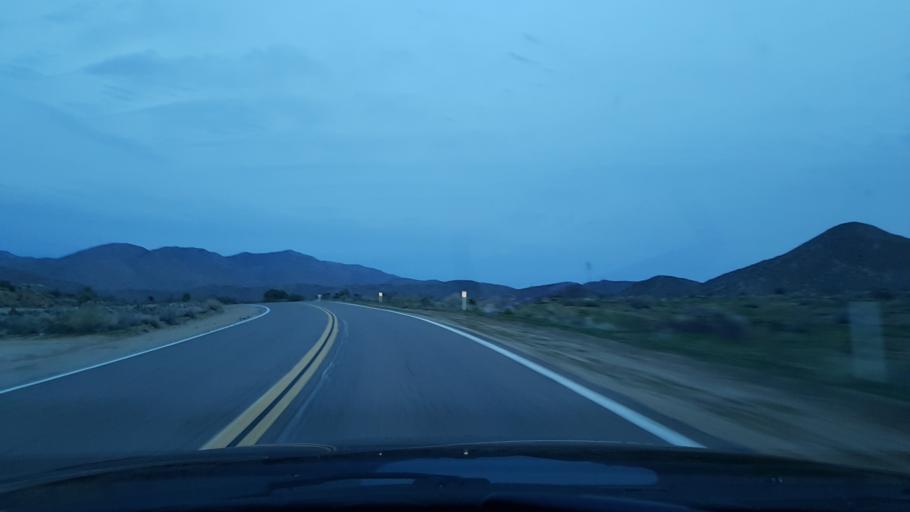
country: US
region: California
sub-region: San Diego County
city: Julian
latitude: 33.0175
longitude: -116.4284
